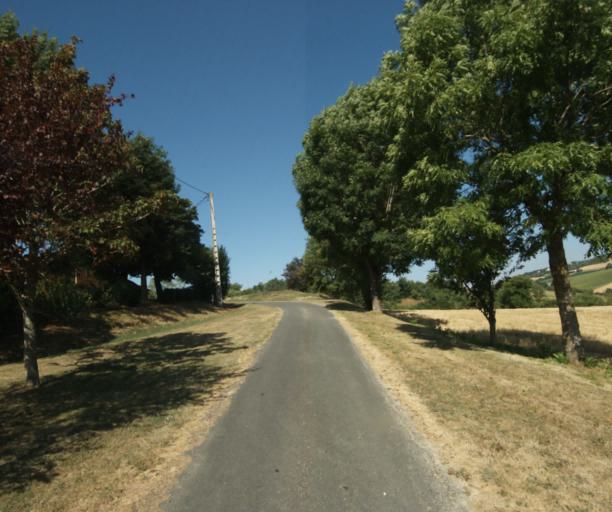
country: FR
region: Midi-Pyrenees
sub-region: Departement de la Haute-Garonne
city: Saint-Felix-Lauragais
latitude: 43.5044
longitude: 1.9372
